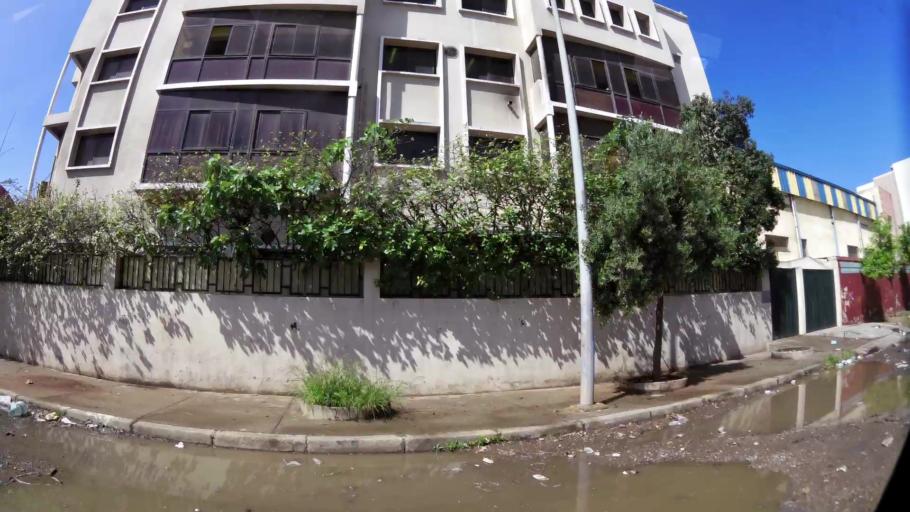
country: MA
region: Grand Casablanca
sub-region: Mediouna
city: Tit Mellil
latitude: 33.6195
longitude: -7.5032
